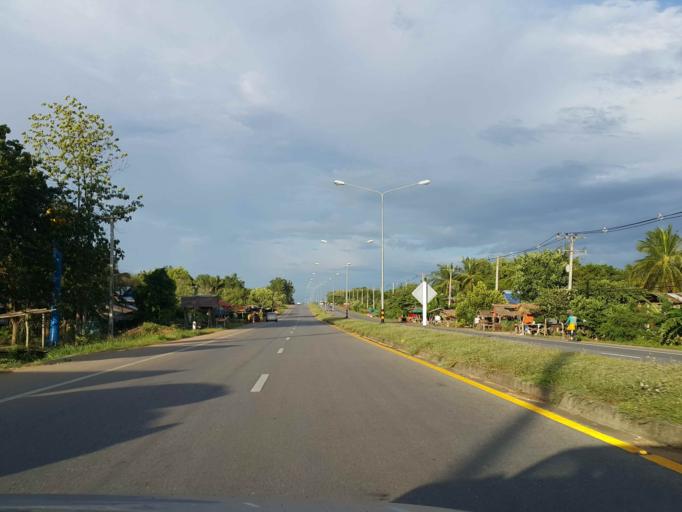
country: TH
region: Sukhothai
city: Ban Dan Lan Hoi
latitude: 16.9256
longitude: 99.4058
